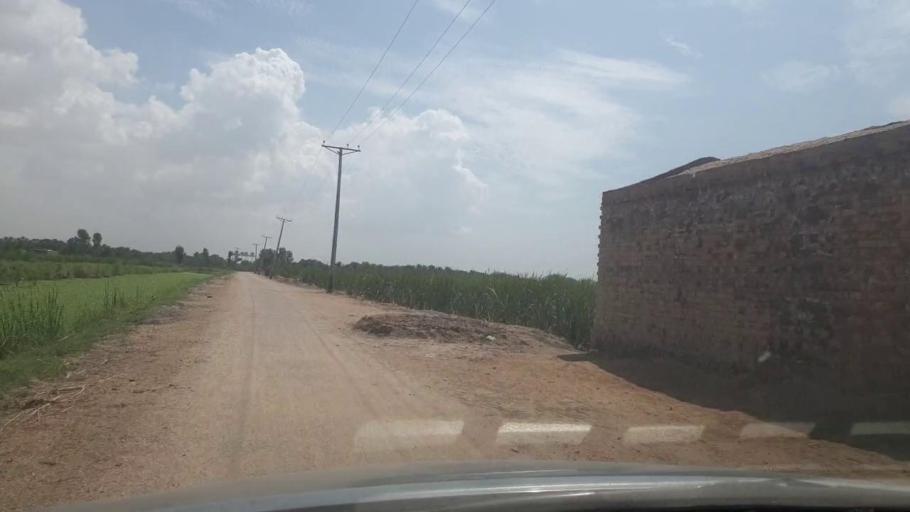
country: PK
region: Sindh
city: Khairpur
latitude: 27.4786
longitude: 68.8107
